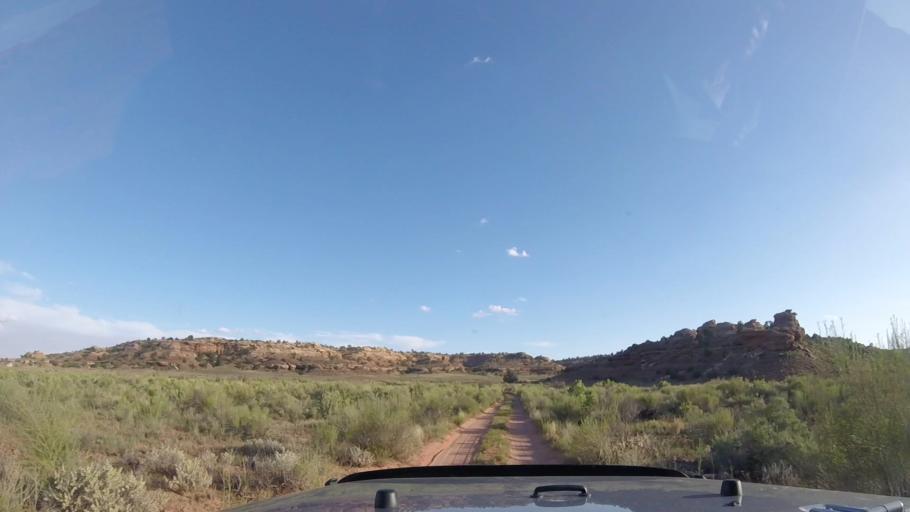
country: US
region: Utah
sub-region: Grand County
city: Moab
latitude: 38.1943
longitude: -109.7842
